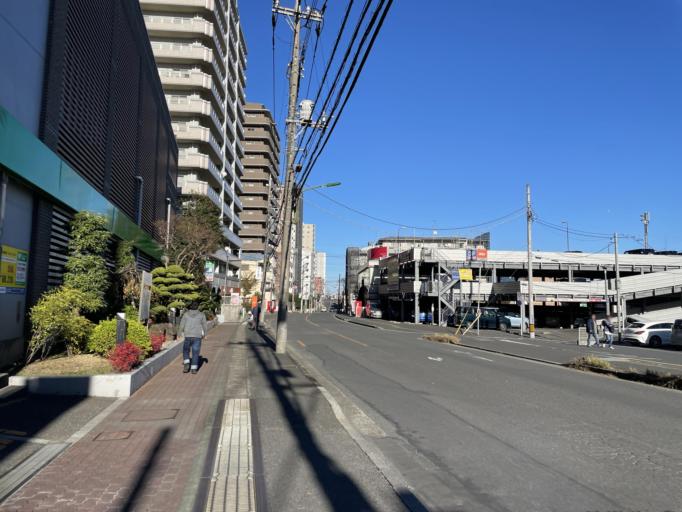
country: JP
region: Saitama
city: Asaka
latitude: 35.8123
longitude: 139.5849
